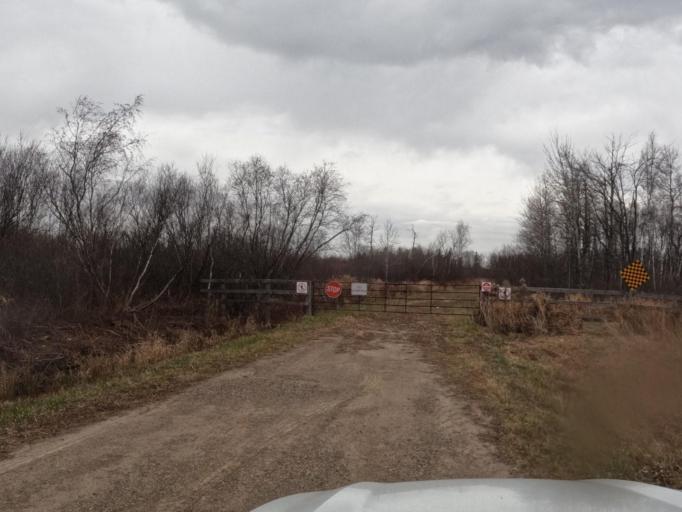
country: CA
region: Ontario
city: Shelburne
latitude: 43.8977
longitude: -80.3848
